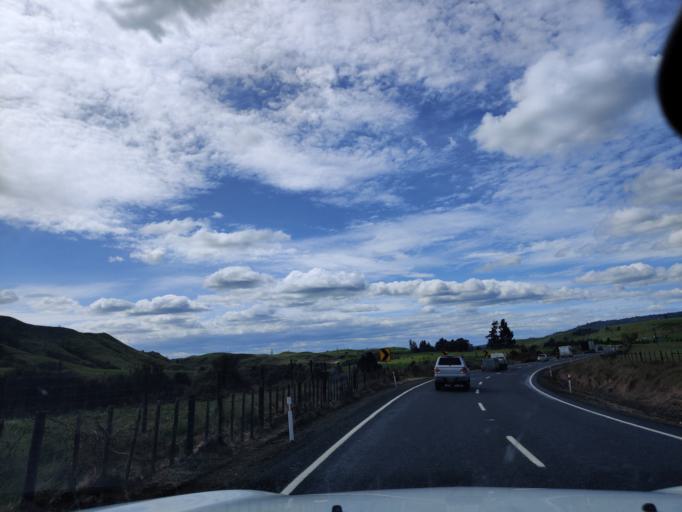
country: NZ
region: Waikato
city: Turangi
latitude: -39.0945
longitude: 175.3762
